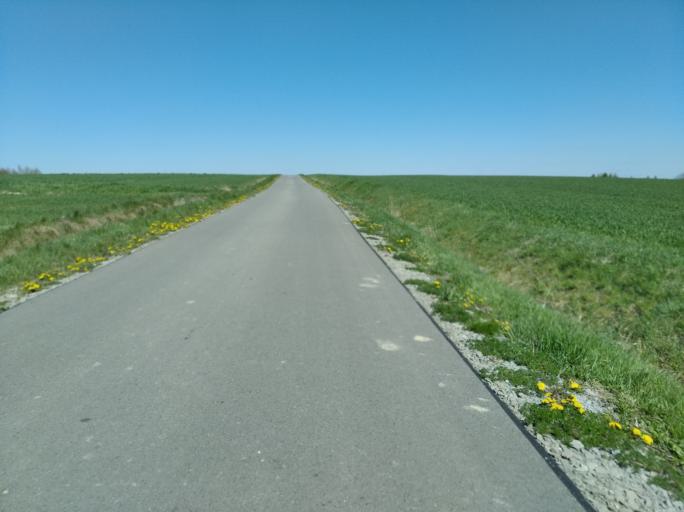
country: PL
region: Subcarpathian Voivodeship
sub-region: Powiat strzyzowski
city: Wisniowa
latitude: 49.9038
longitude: 21.6864
